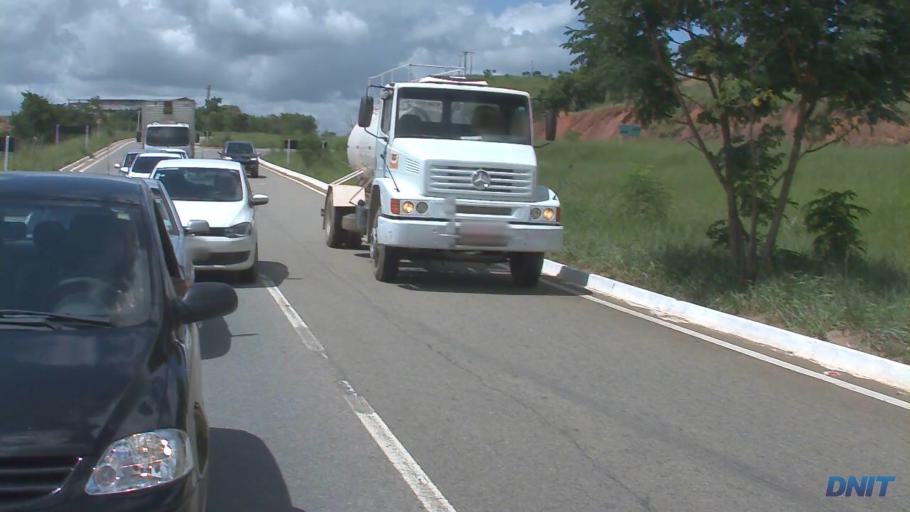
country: BR
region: Minas Gerais
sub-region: Governador Valadares
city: Governador Valadares
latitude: -18.9068
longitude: -42.0043
